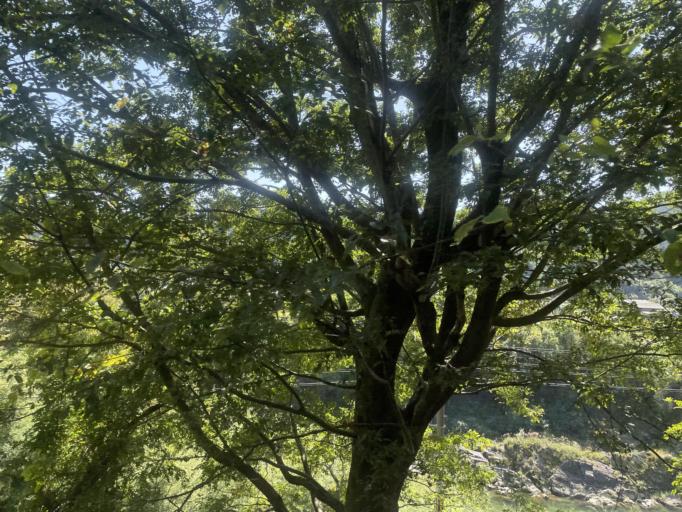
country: JP
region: Nara
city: Gose
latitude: 34.3824
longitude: 135.7760
